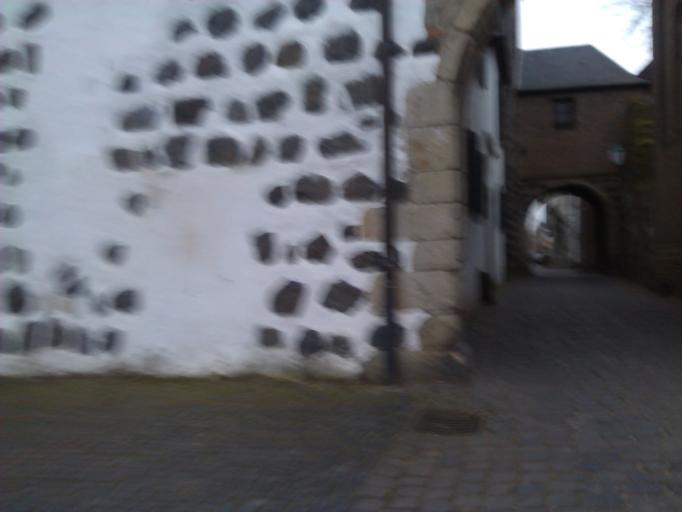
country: DE
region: North Rhine-Westphalia
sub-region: Regierungsbezirk Dusseldorf
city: Dormagen
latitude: 51.1229
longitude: 6.8511
